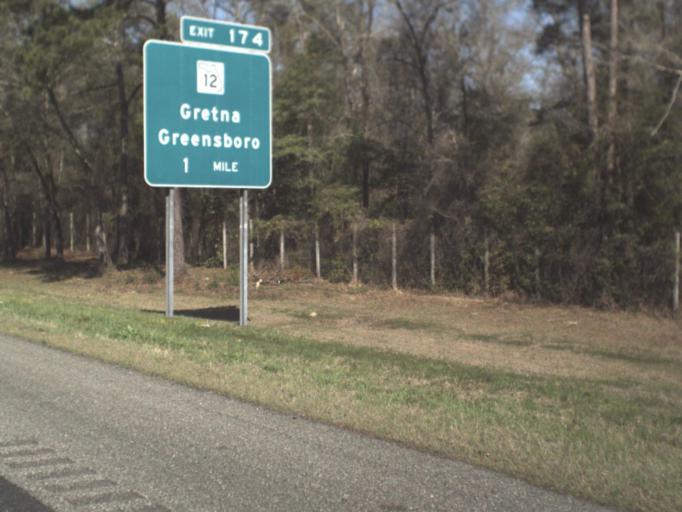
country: US
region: Florida
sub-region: Gadsden County
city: Gretna
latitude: 30.5722
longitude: -84.6787
